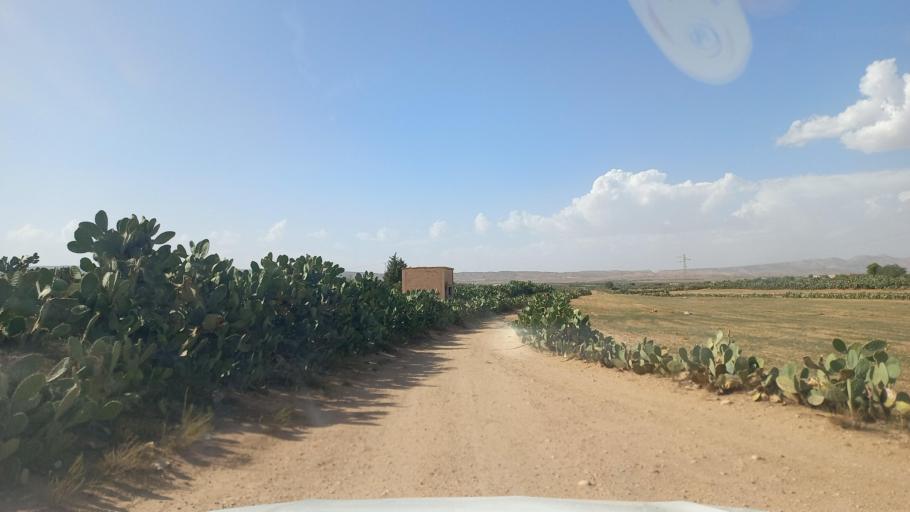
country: TN
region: Al Qasrayn
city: Sbiba
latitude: 35.3074
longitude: 9.0351
